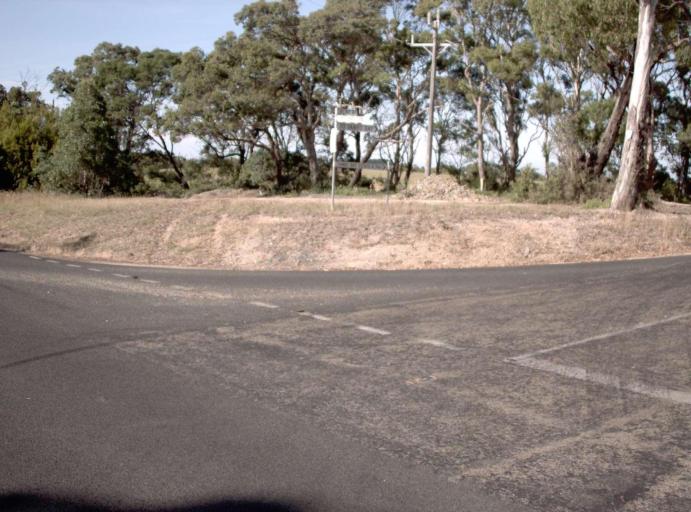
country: AU
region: Victoria
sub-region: East Gippsland
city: Lakes Entrance
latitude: -37.8577
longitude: 147.8453
